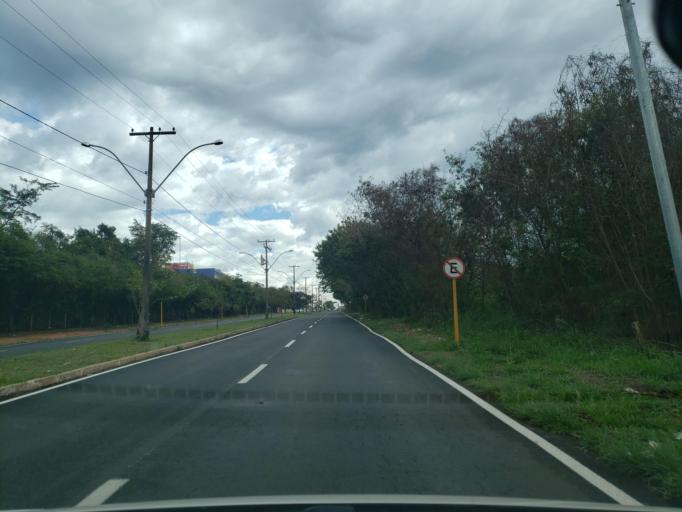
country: BR
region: Sao Paulo
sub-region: Bauru
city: Bauru
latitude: -22.3398
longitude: -49.0250
